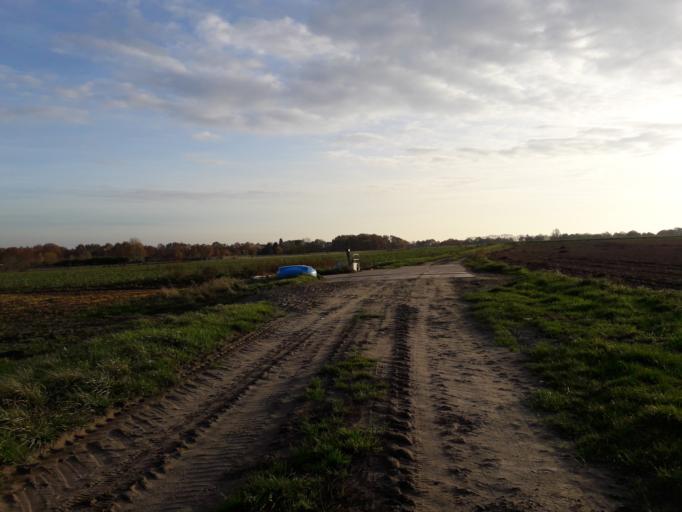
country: NL
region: Drenthe
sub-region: Gemeente Borger-Odoorn
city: Borger
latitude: 52.9544
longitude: 6.8177
